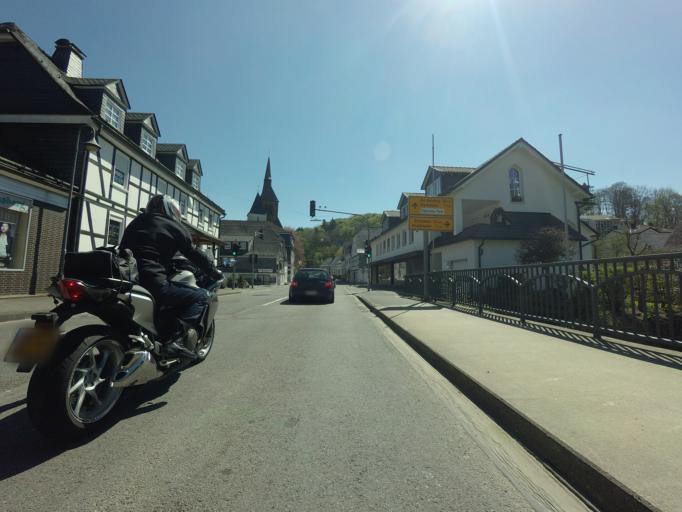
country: DE
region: North Rhine-Westphalia
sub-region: Regierungsbezirk Arnsberg
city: Kirchhundem
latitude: 51.0865
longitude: 8.0890
